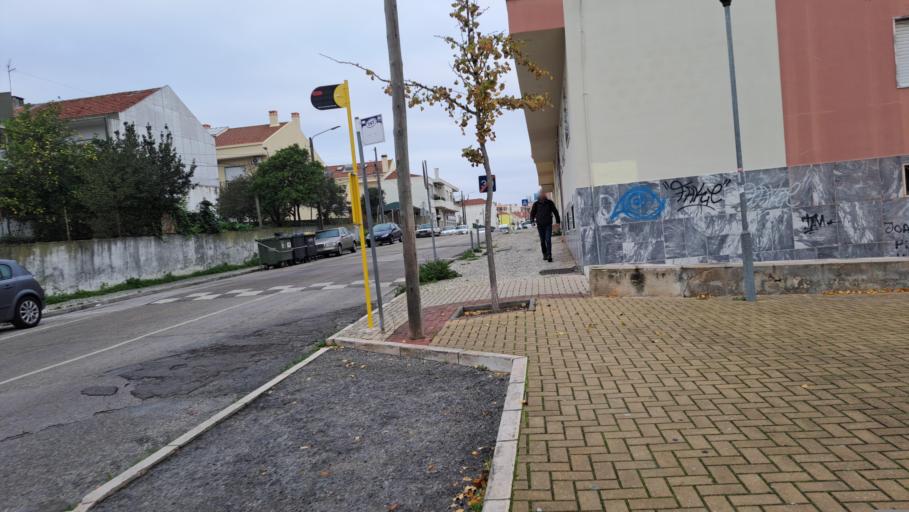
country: PT
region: Setubal
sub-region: Moita
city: Alhos Vedros
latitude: 38.6503
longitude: -9.0453
